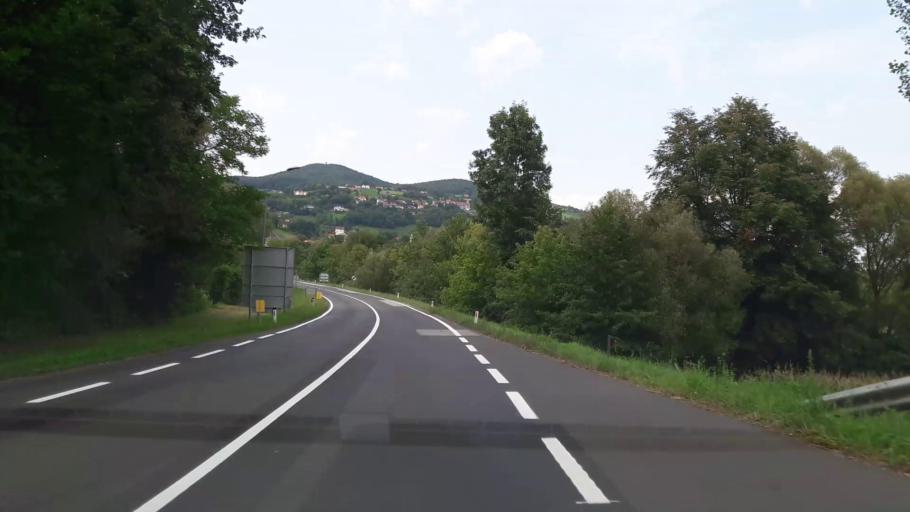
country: AT
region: Styria
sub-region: Politischer Bezirk Hartberg-Fuerstenfeld
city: Hartberg
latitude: 47.2708
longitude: 15.9711
